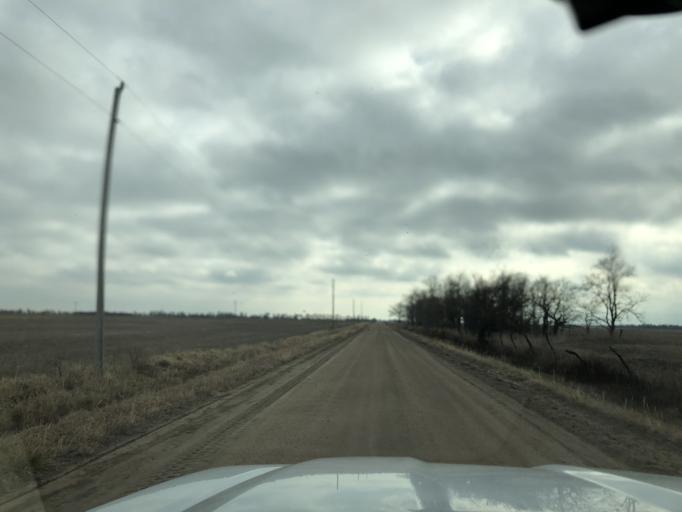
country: US
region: Kansas
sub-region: Reno County
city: Nickerson
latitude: 38.0020
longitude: -98.2158
